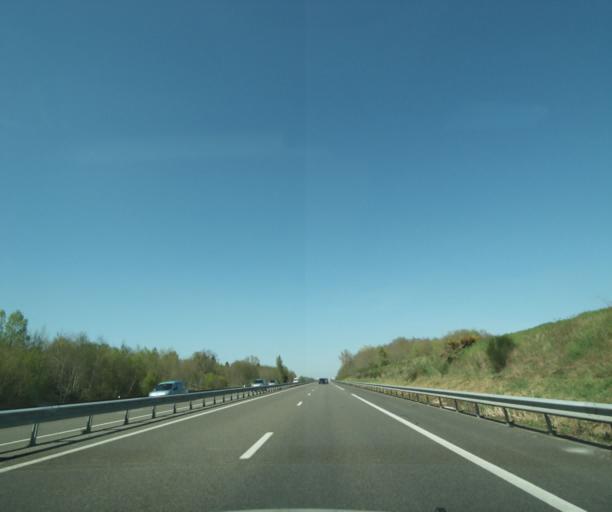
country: FR
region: Bourgogne
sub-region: Departement de la Nievre
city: Cosne-Cours-sur-Loire
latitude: 47.3672
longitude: 2.9234
